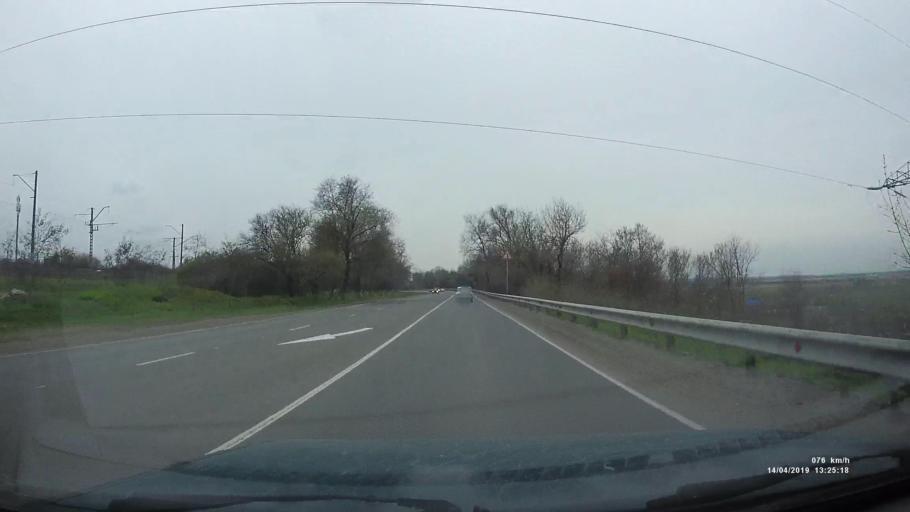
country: RU
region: Rostov
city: Azov
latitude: 47.0862
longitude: 39.4709
